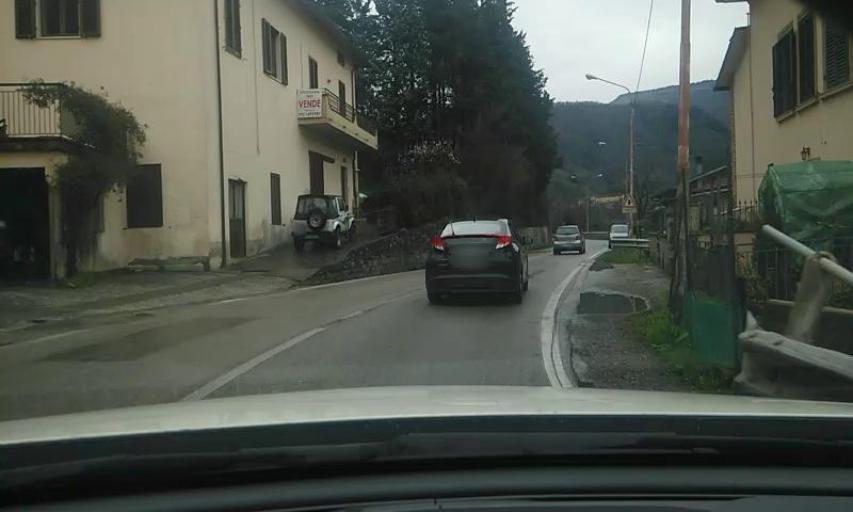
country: IT
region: Tuscany
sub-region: Provincia di Prato
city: Vaiano
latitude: 43.9370
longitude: 11.1258
